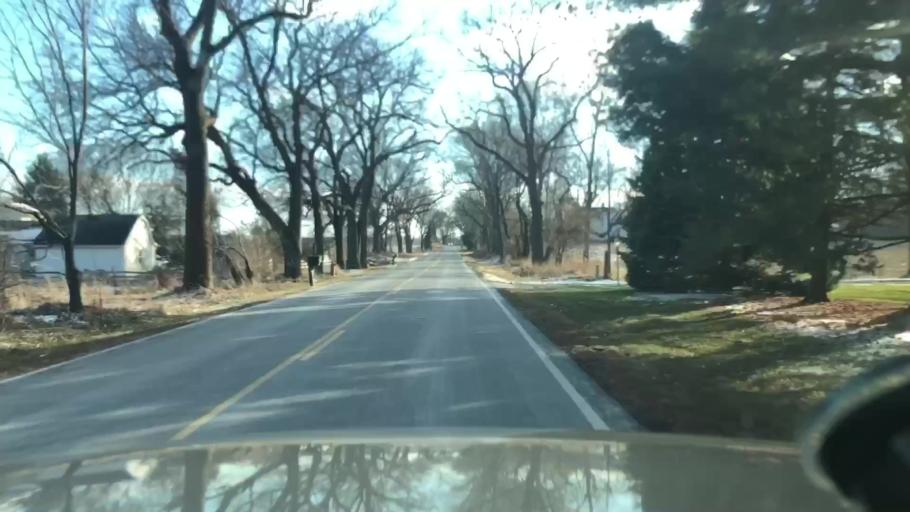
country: US
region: Michigan
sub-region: Jackson County
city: Vandercook Lake
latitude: 42.1713
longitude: -84.4521
